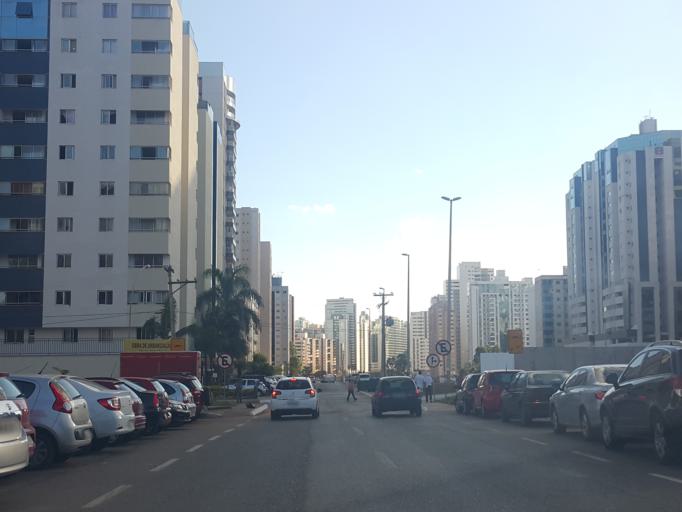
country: BR
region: Federal District
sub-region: Brasilia
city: Brasilia
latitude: -15.8371
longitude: -48.0172
